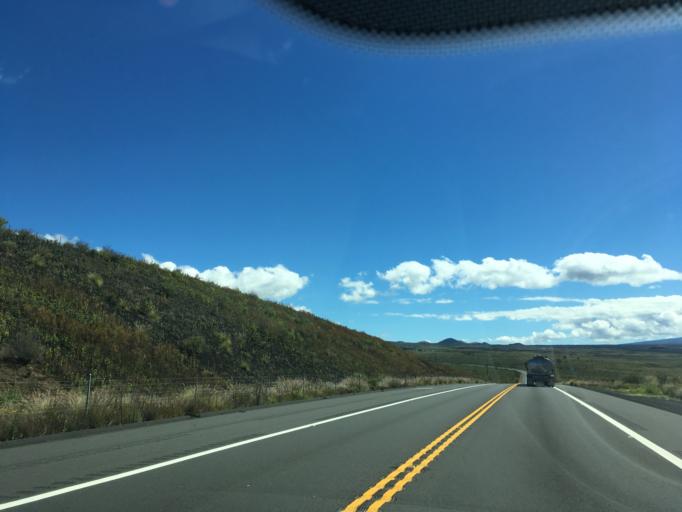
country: US
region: Hawaii
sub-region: Hawaii County
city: Waikoloa
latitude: 19.7747
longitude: -155.5918
